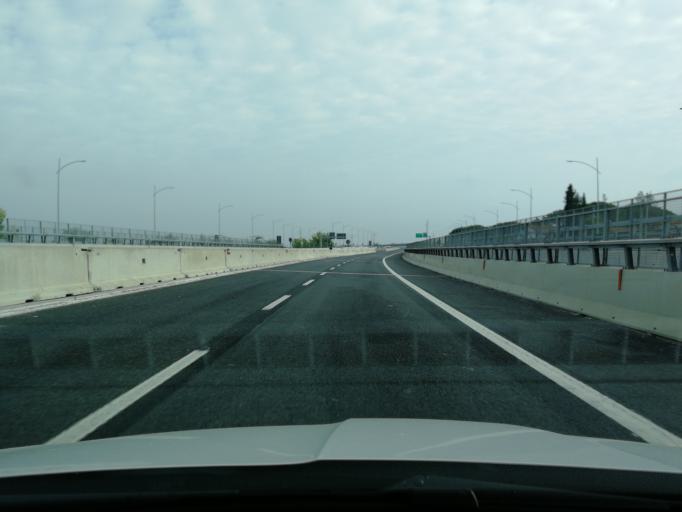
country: IT
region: Latium
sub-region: Citta metropolitana di Roma Capitale
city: Setteville
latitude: 41.9221
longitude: 12.6506
